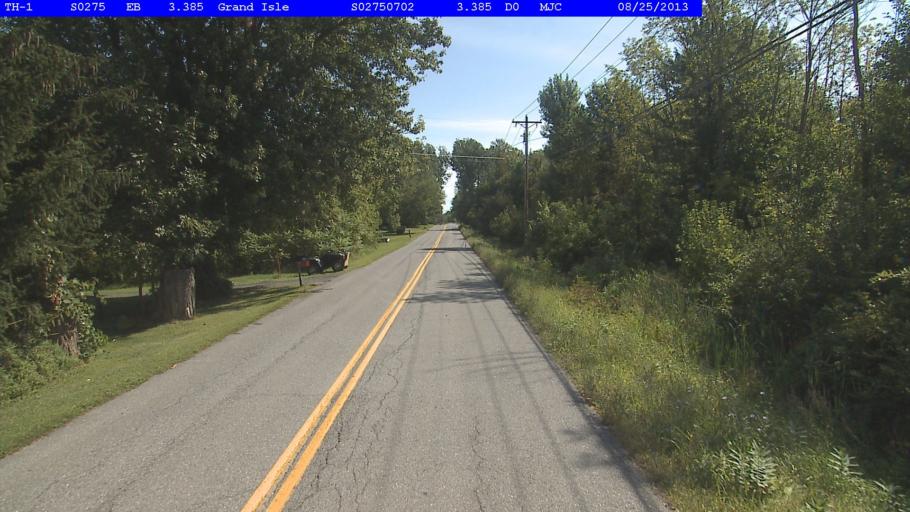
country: US
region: Vermont
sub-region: Grand Isle County
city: North Hero
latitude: 44.7353
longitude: -73.3133
